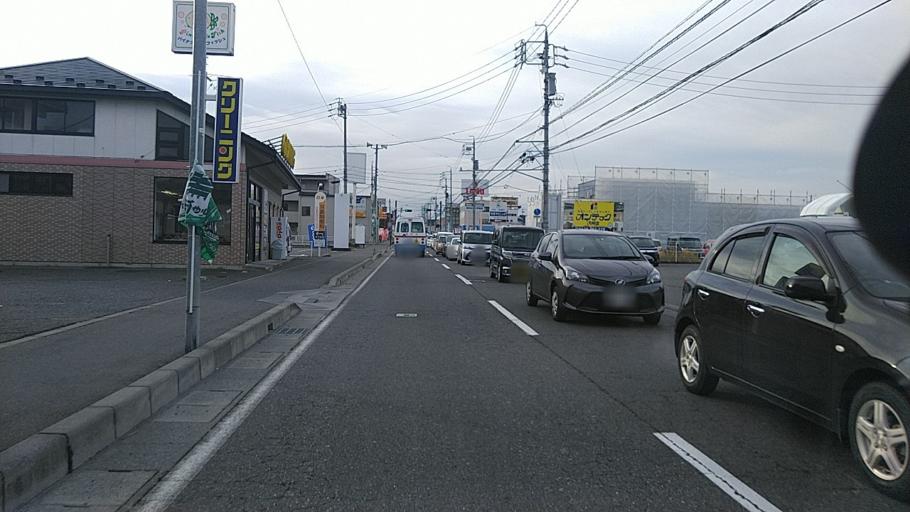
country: JP
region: Nagano
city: Matsumoto
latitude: 36.2111
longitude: 137.9795
